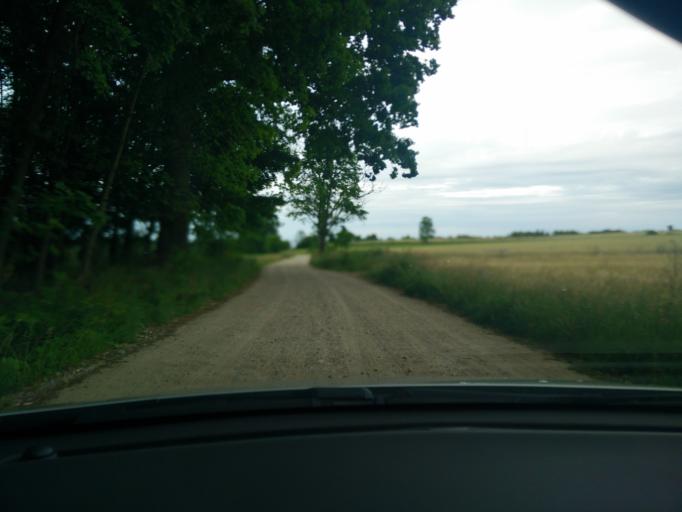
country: PL
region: Pomeranian Voivodeship
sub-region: Powiat pucki
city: Mrzezino
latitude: 54.6606
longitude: 18.4506
